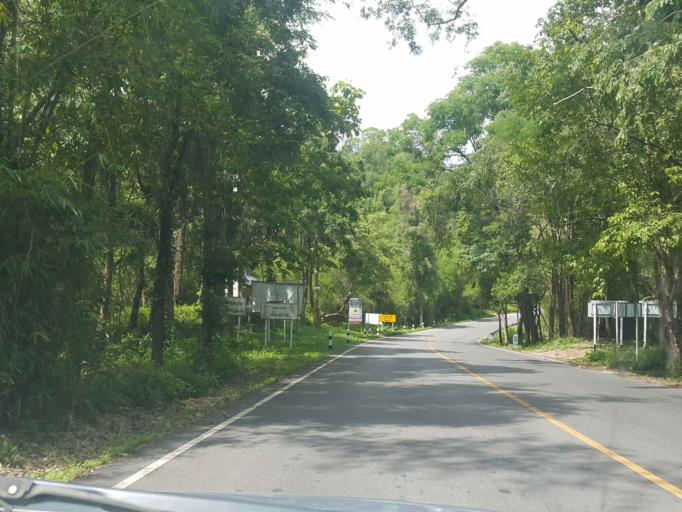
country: TH
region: Nan
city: Ban Luang
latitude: 18.8742
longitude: 100.5297
